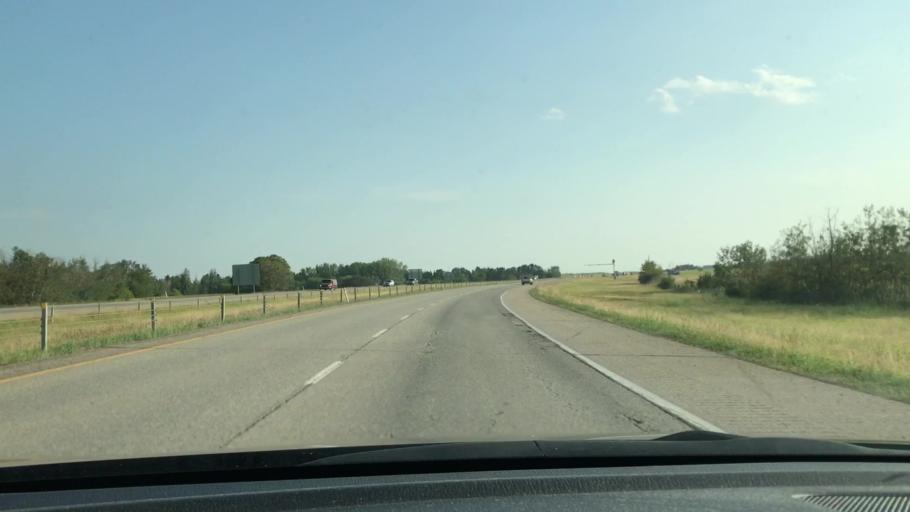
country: CA
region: Alberta
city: Leduc
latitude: 53.2433
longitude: -113.5623
